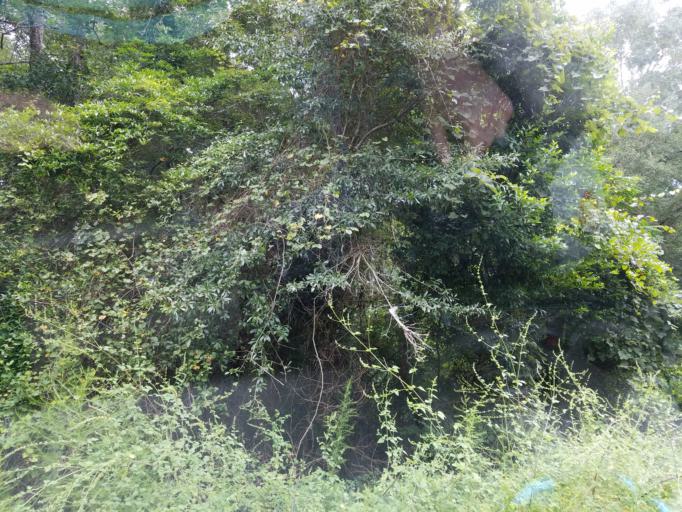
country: US
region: Mississippi
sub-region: Perry County
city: Richton
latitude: 31.3566
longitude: -88.8166
